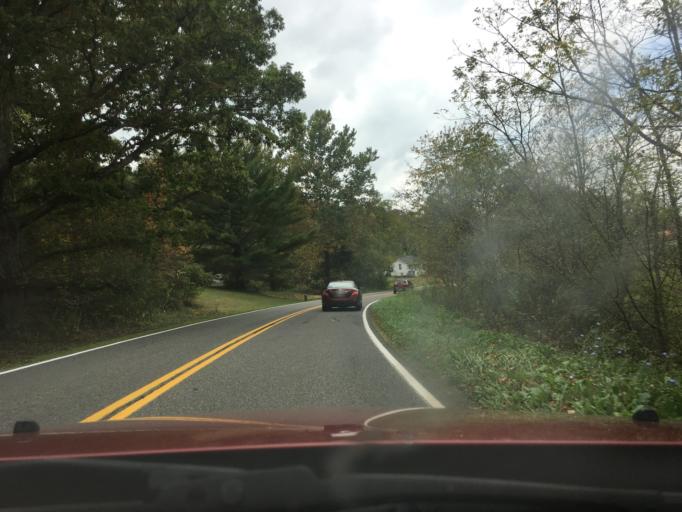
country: US
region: Virginia
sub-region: Pulaski County
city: Fairlawn
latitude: 37.1702
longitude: -80.6059
